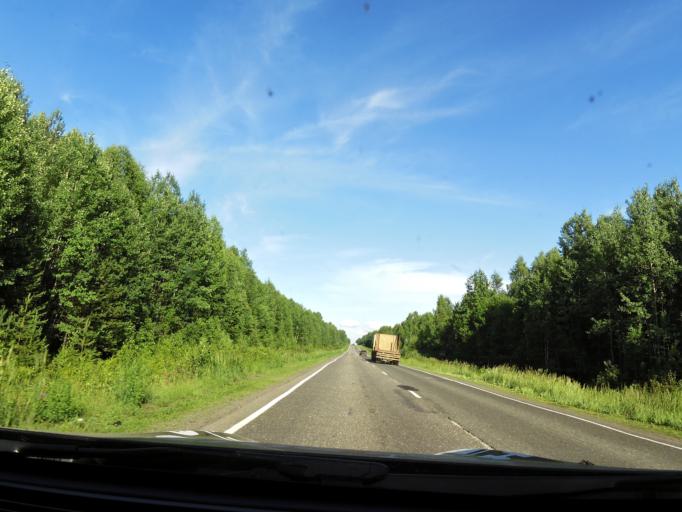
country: RU
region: Kirov
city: Chernaya Kholunitsa
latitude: 58.8808
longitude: 51.4378
